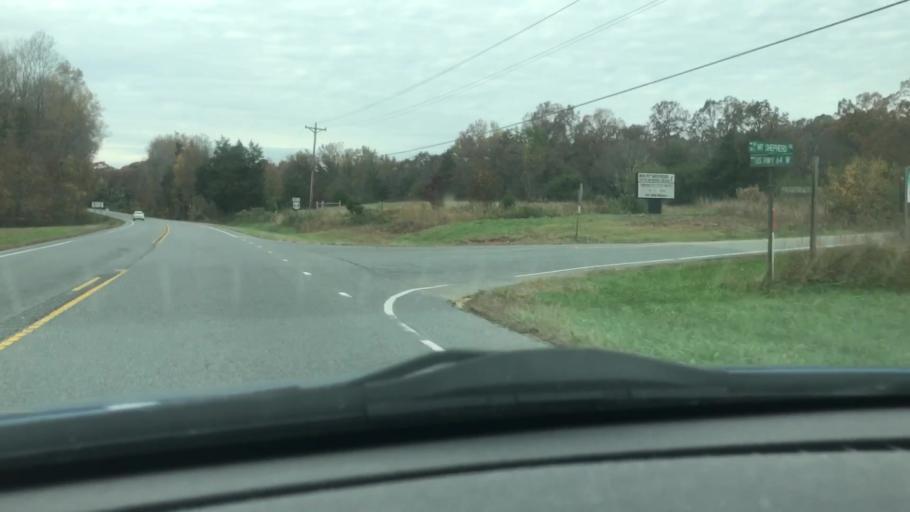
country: US
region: North Carolina
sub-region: Randolph County
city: Asheboro
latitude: 35.7313
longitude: -79.9442
